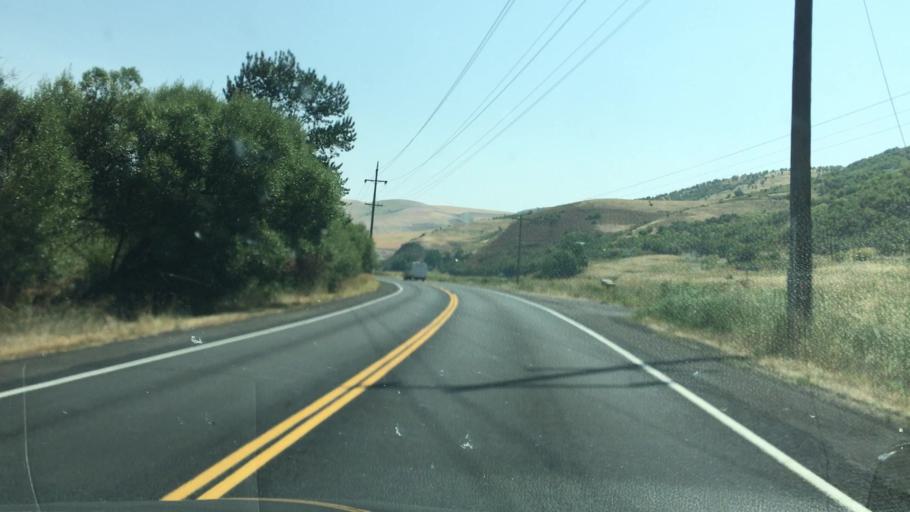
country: US
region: Idaho
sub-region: Nez Perce County
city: Lapwai
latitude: 46.3583
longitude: -116.7885
